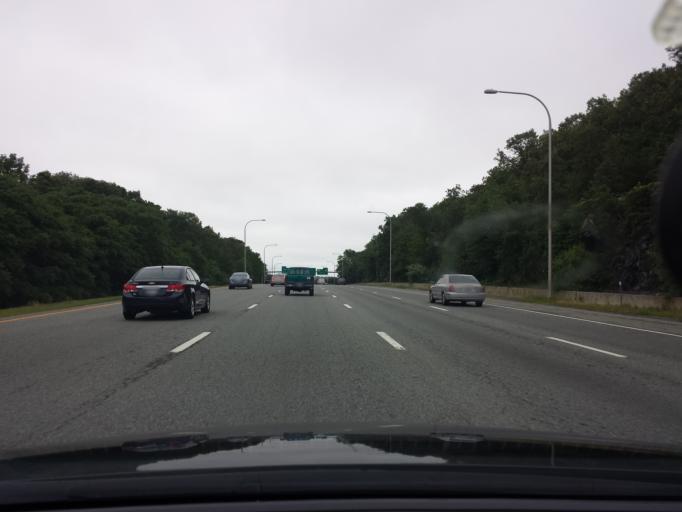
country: US
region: Rhode Island
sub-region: Kent County
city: East Greenwich
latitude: 41.7046
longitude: -71.4729
